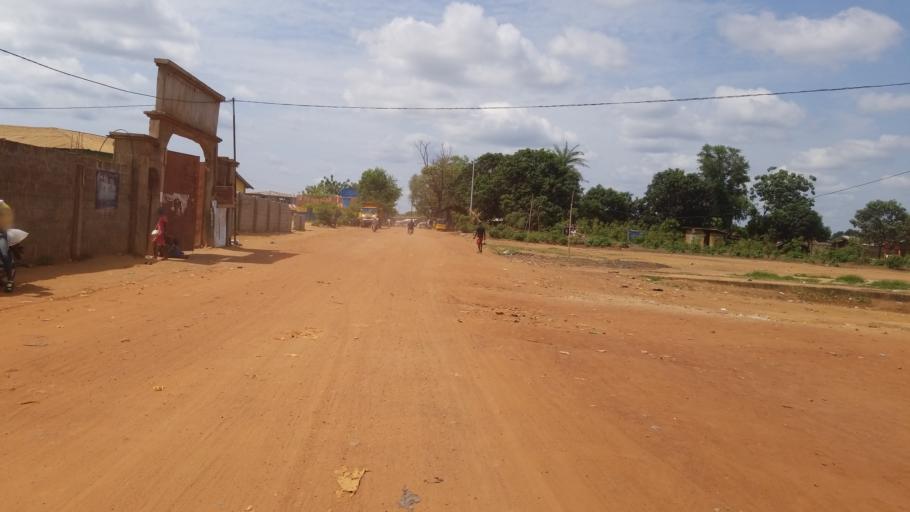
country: SL
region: Western Area
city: Waterloo
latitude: 8.3248
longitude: -13.0640
